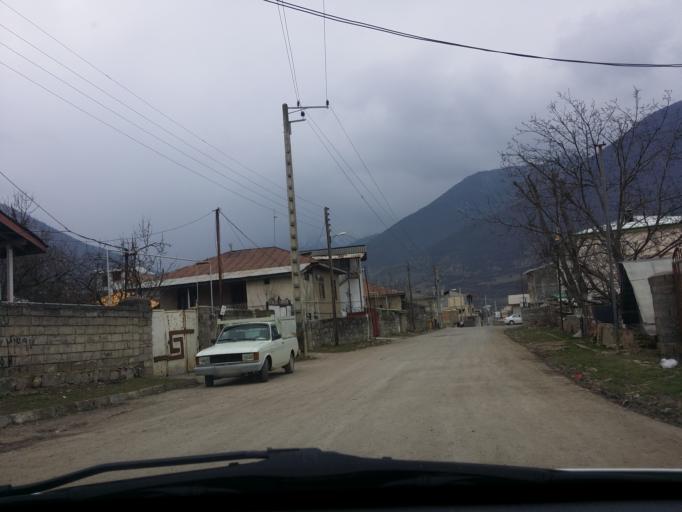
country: IR
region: Mazandaran
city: `Abbasabad
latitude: 36.4914
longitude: 51.1507
